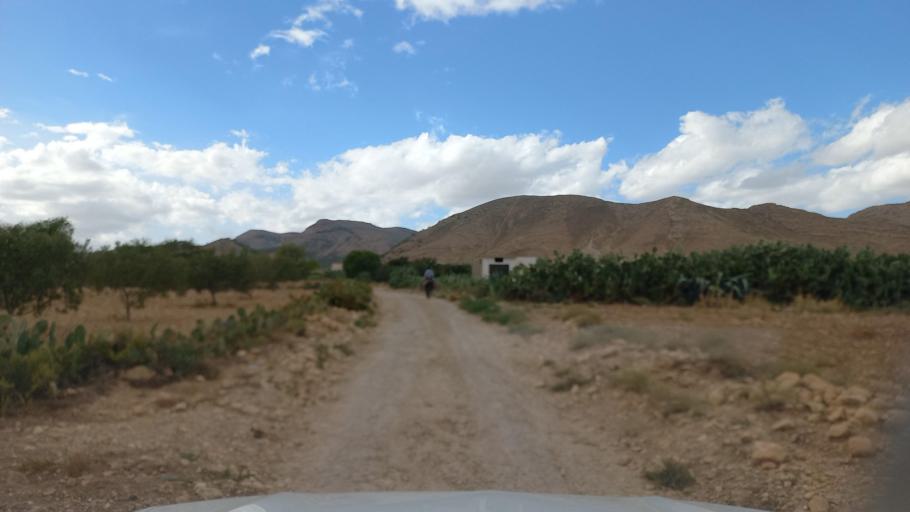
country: TN
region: Al Qasrayn
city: Sbiba
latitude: 35.4490
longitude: 9.0719
